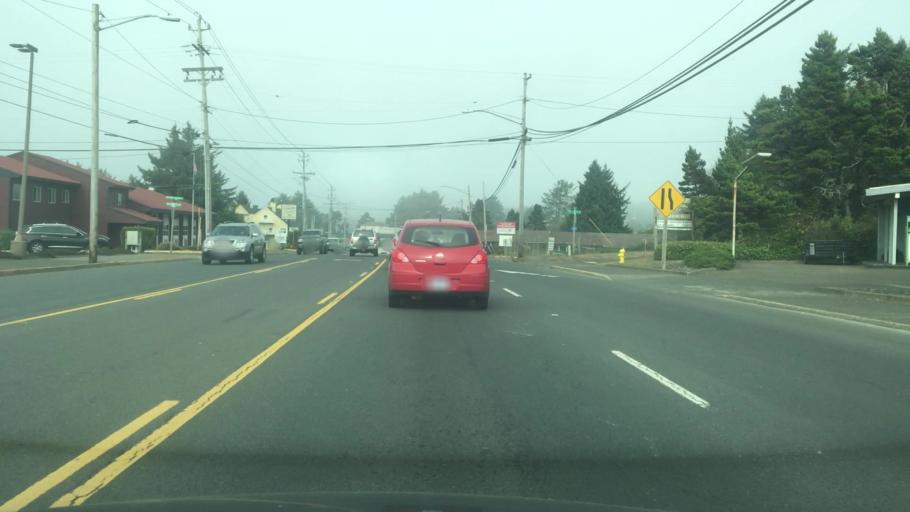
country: US
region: Oregon
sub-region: Lincoln County
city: Lincoln City
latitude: 44.9829
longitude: -124.0072
